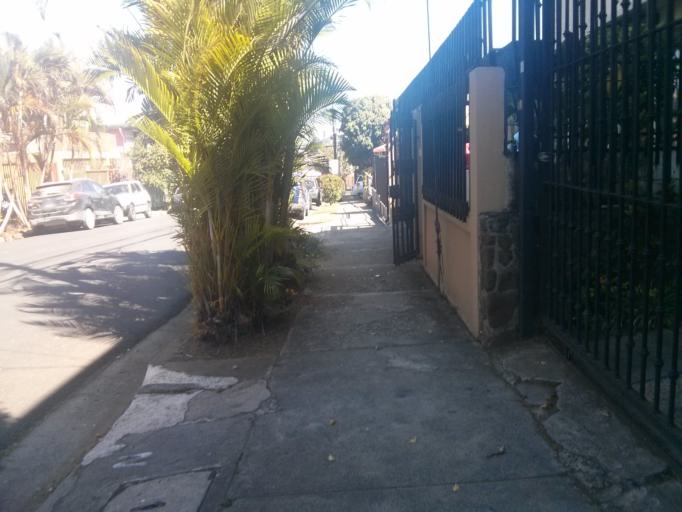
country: CR
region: San Jose
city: San Pedro
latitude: 9.9285
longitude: -84.0466
